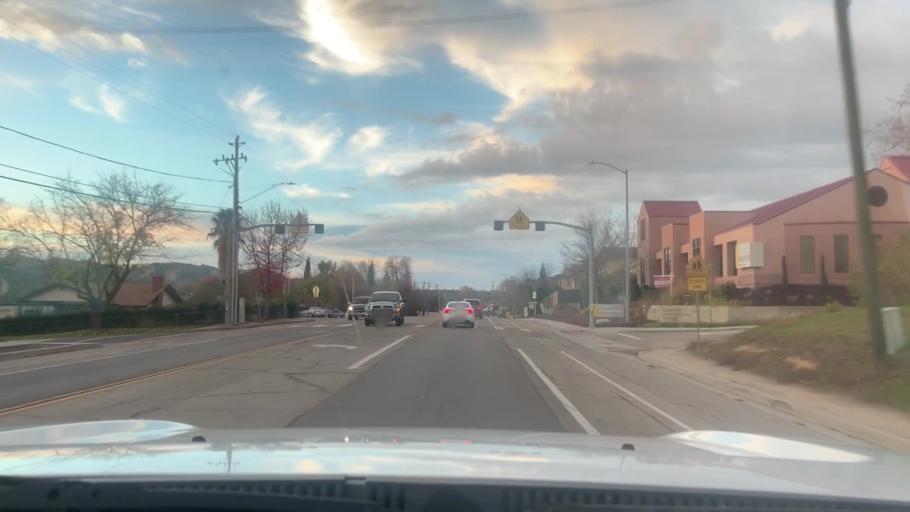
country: US
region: California
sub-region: San Luis Obispo County
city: Paso Robles
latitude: 35.6262
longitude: -120.6721
